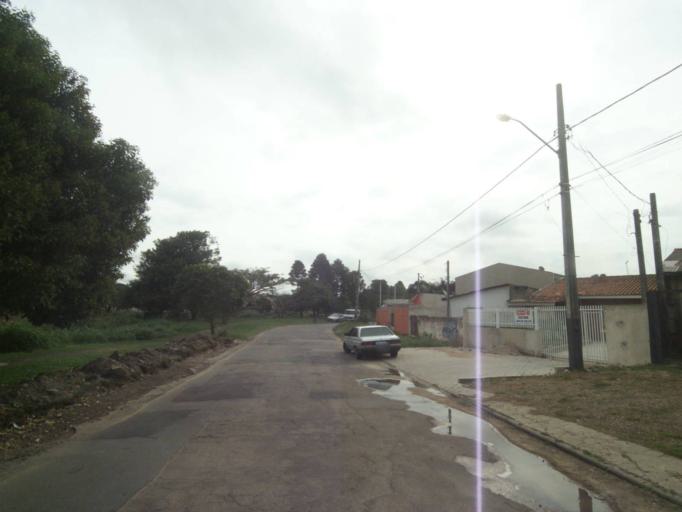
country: BR
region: Parana
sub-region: Sao Jose Dos Pinhais
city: Sao Jose dos Pinhais
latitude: -25.5539
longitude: -49.2692
